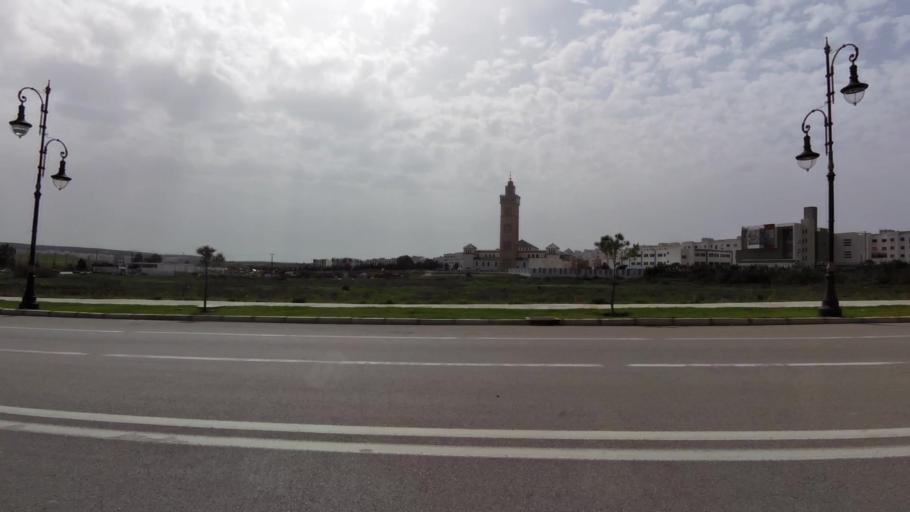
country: MA
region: Tanger-Tetouan
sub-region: Tanger-Assilah
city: Boukhalef
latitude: 35.7333
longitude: -5.8743
